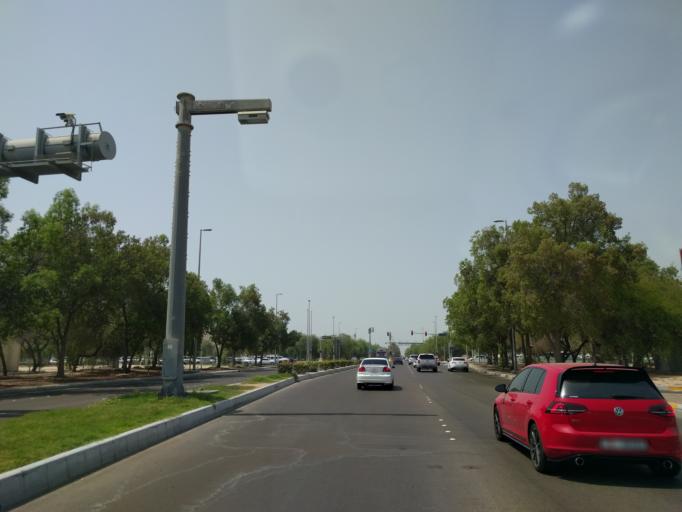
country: AE
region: Abu Dhabi
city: Abu Dhabi
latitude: 24.4328
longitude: 54.4299
